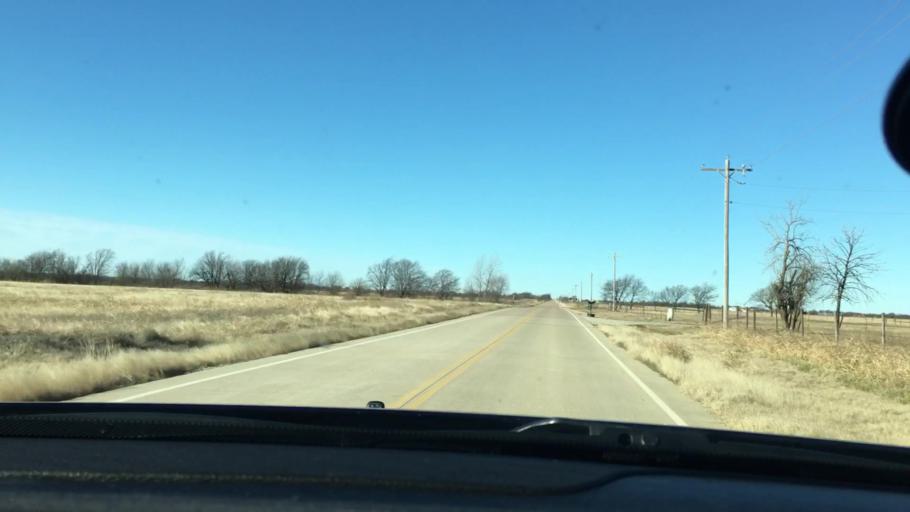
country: US
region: Oklahoma
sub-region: Marshall County
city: Madill
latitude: 34.1145
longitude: -96.6903
